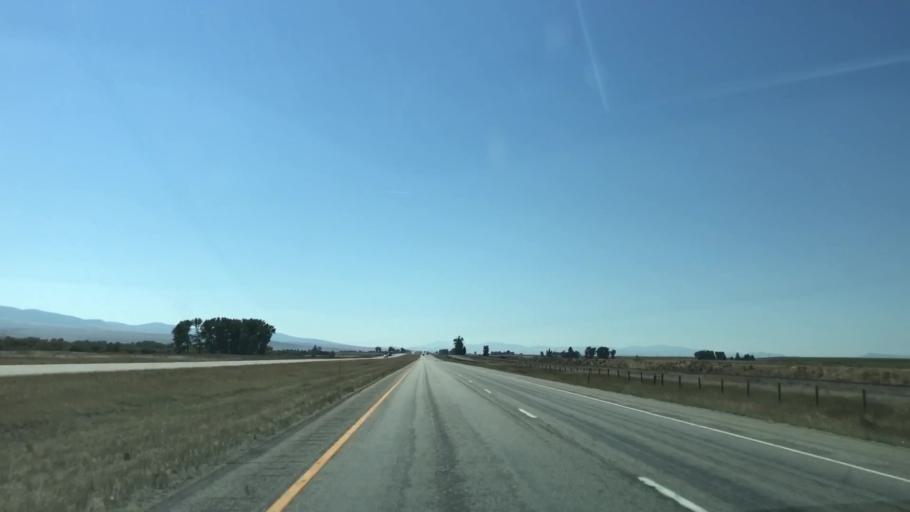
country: US
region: Montana
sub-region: Powell County
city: Deer Lodge
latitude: 46.3367
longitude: -112.7430
